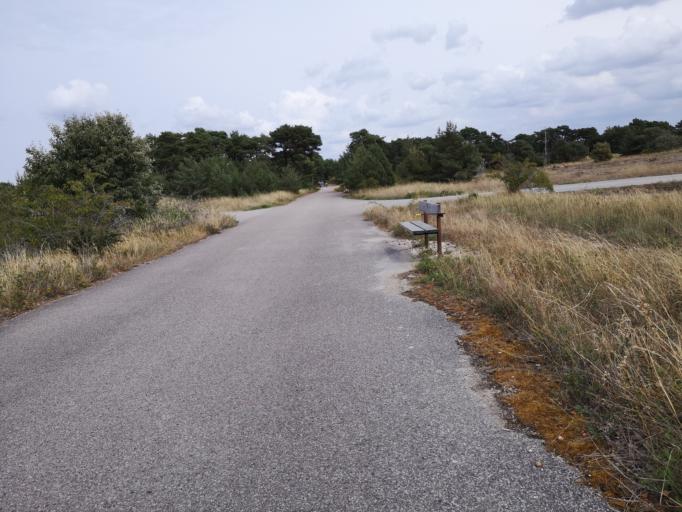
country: SE
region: Gotland
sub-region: Gotland
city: Vibble
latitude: 57.6125
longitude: 18.2584
